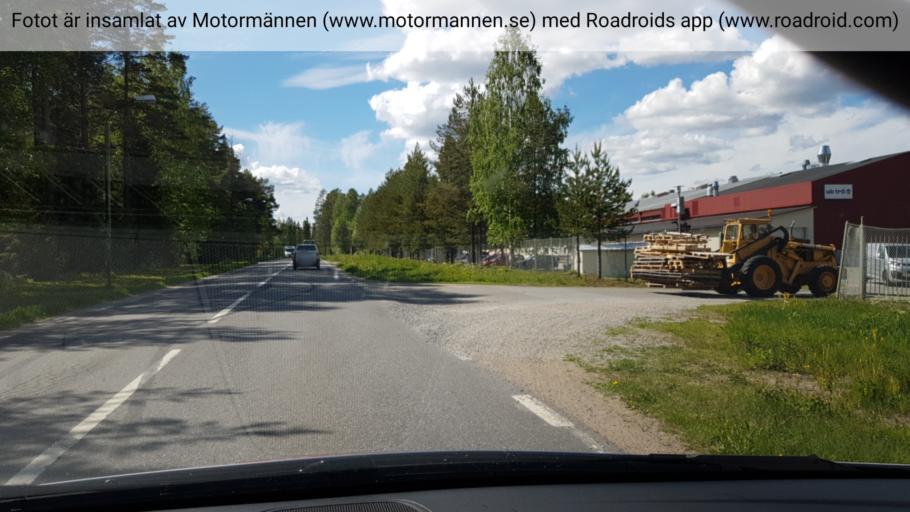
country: SE
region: Vaesterbotten
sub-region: Skelleftea Kommun
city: Burtraesk
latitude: 64.5122
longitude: 20.6325
